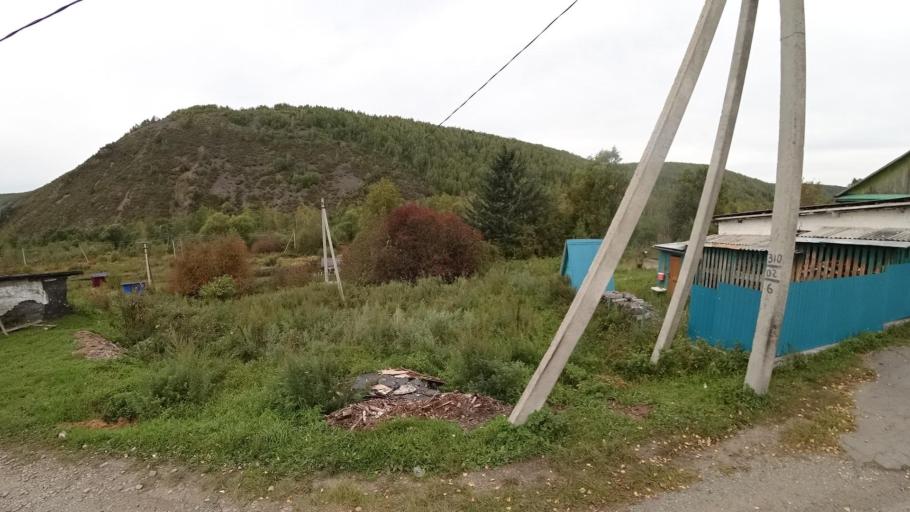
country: RU
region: Jewish Autonomous Oblast
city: Khingansk
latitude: 49.1310
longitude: 131.2002
